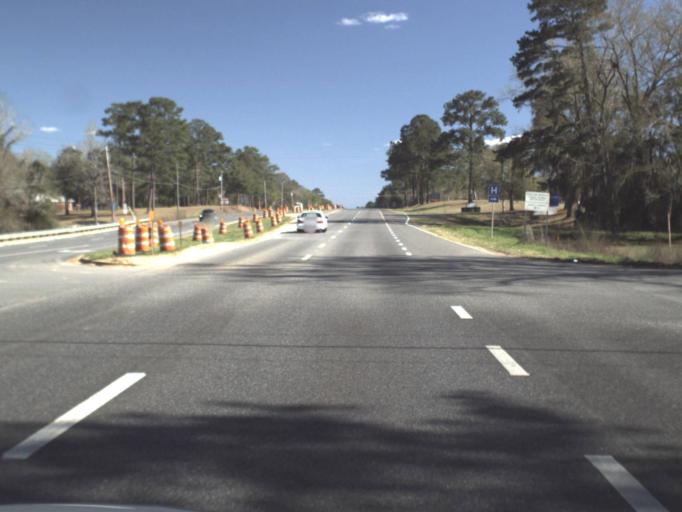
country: US
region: Florida
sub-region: Gadsden County
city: Quincy
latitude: 30.5714
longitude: -84.5501
